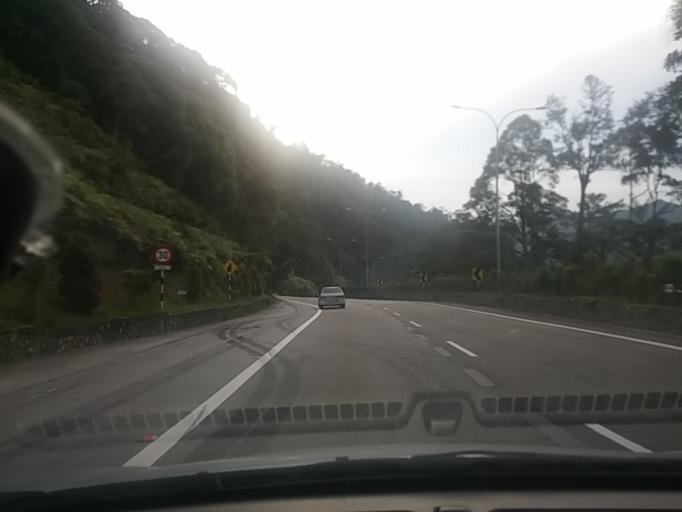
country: MY
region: Pahang
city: Kampung Bukit Tinggi, Bentong
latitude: 3.3685
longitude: 101.7791
